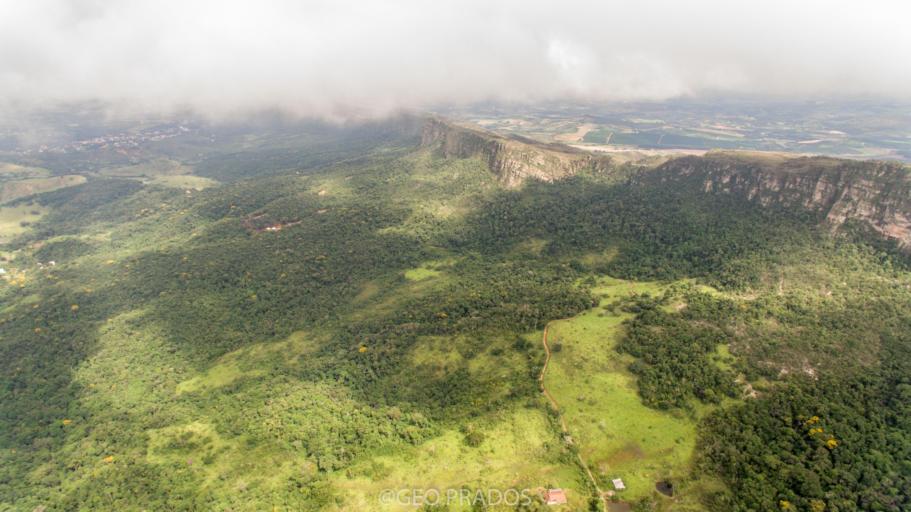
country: BR
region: Minas Gerais
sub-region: Tiradentes
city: Tiradentes
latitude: -21.0699
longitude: -44.1229
